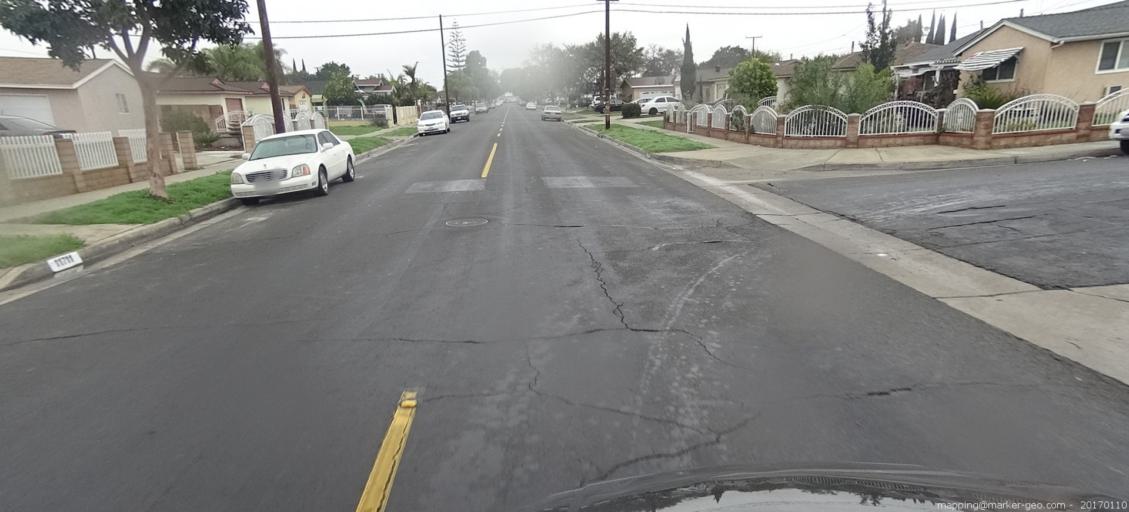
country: US
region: California
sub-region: Orange County
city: Stanton
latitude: 33.7923
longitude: -117.9880
